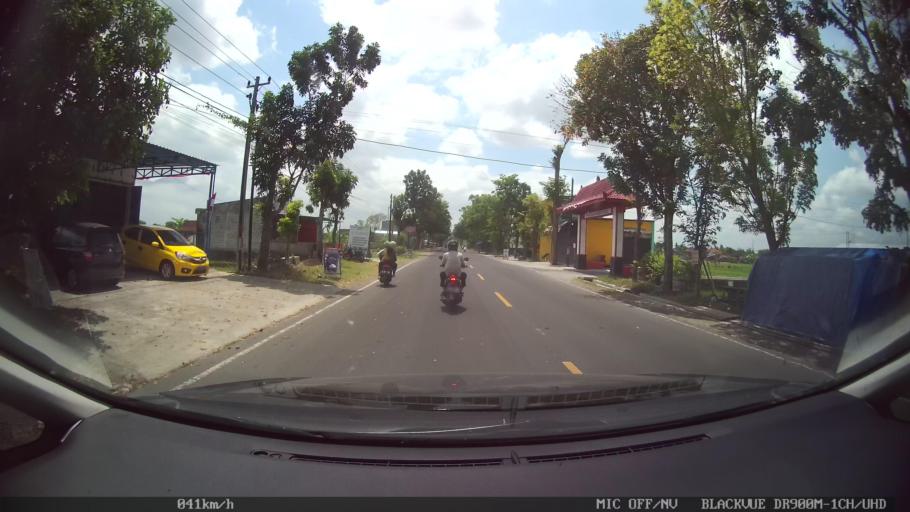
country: ID
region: Daerah Istimewa Yogyakarta
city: Bantul
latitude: -7.9020
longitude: 110.3457
